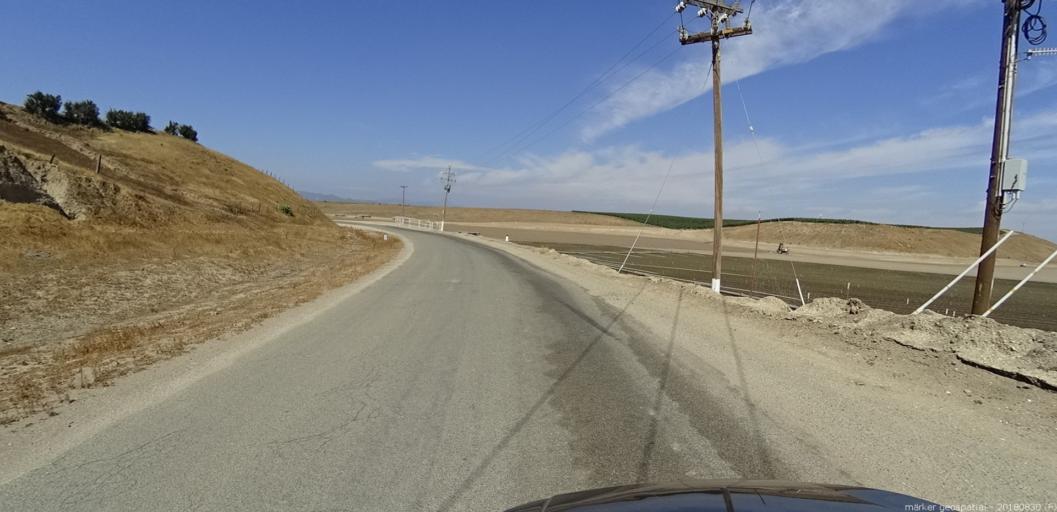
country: US
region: California
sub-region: Monterey County
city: King City
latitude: 36.1123
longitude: -121.0364
